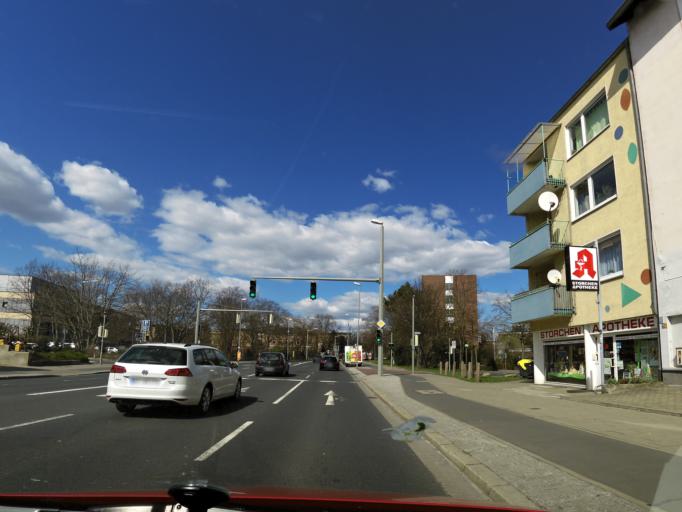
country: DE
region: Lower Saxony
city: Braunschweig
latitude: 52.2737
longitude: 10.5061
